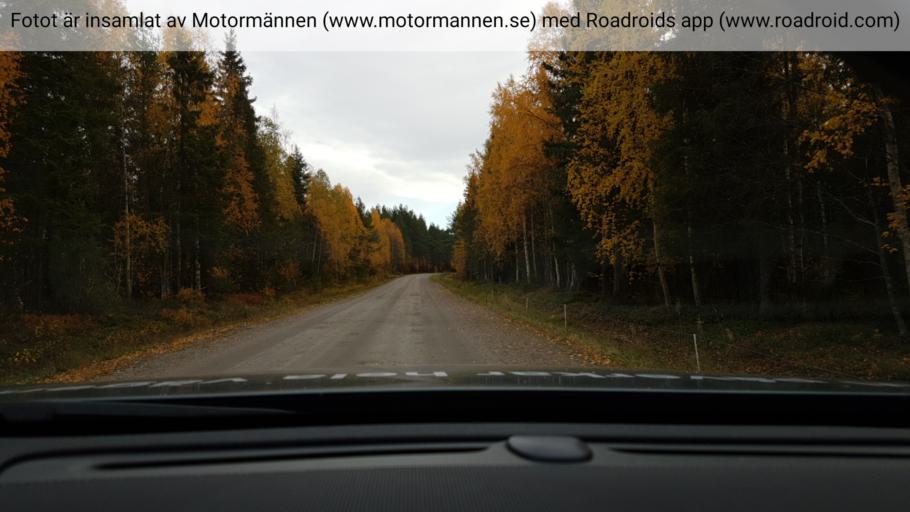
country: SE
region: Norrbotten
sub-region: Overkalix Kommun
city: OEverkalix
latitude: 66.3022
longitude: 22.9307
